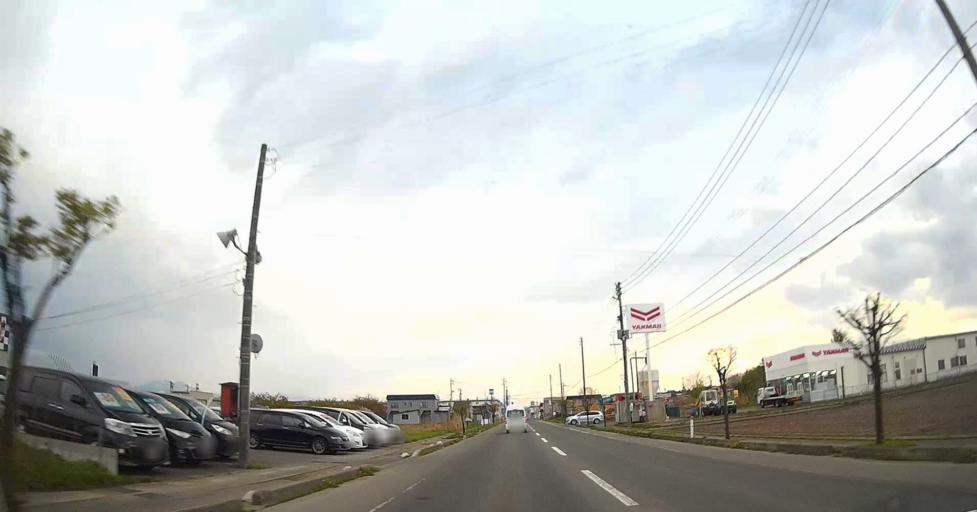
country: JP
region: Aomori
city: Aomori Shi
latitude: 40.8614
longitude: 140.6812
